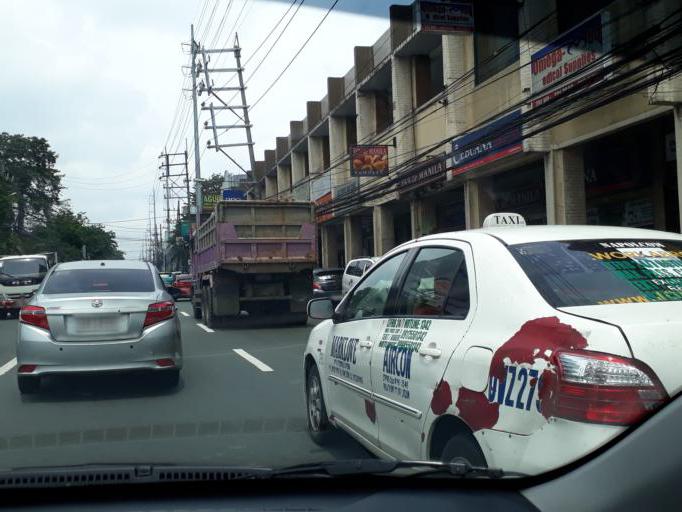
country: PH
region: Calabarzon
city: Del Monte
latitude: 14.6214
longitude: 121.0228
